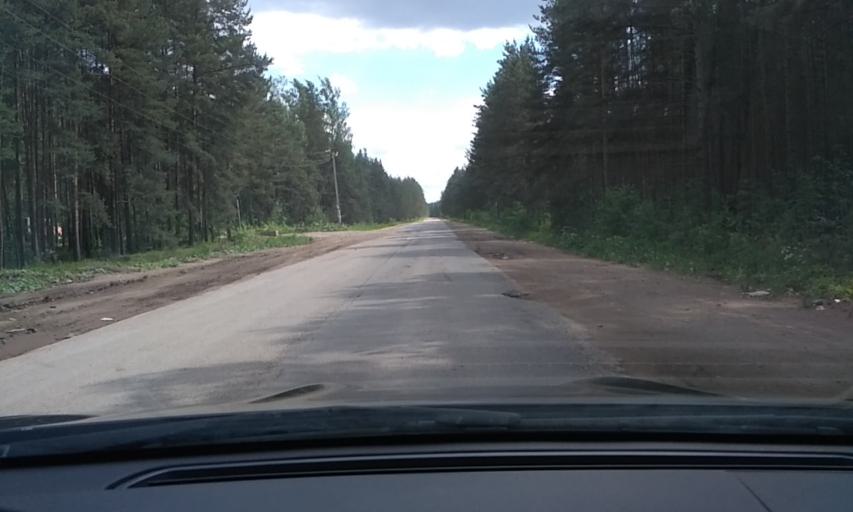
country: RU
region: Leningrad
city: Imeni Sverdlova
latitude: 59.8502
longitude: 30.6807
